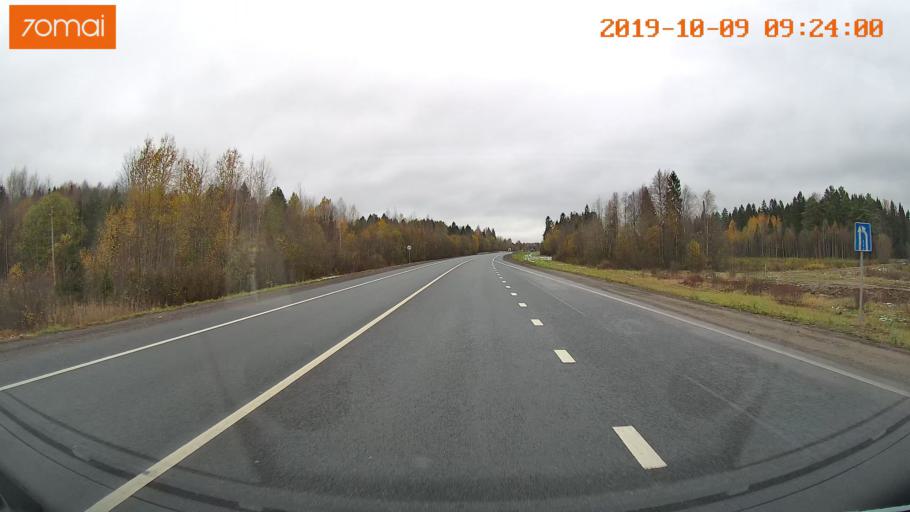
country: RU
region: Vologda
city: Vologda
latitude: 59.0746
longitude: 40.0231
